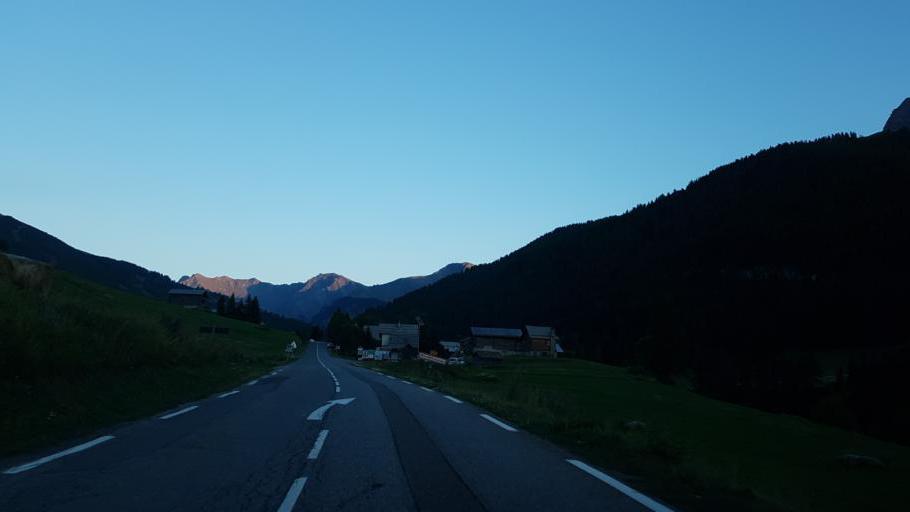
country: FR
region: Provence-Alpes-Cote d'Azur
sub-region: Departement des Hautes-Alpes
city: Guillestre
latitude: 44.7372
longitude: 6.8337
